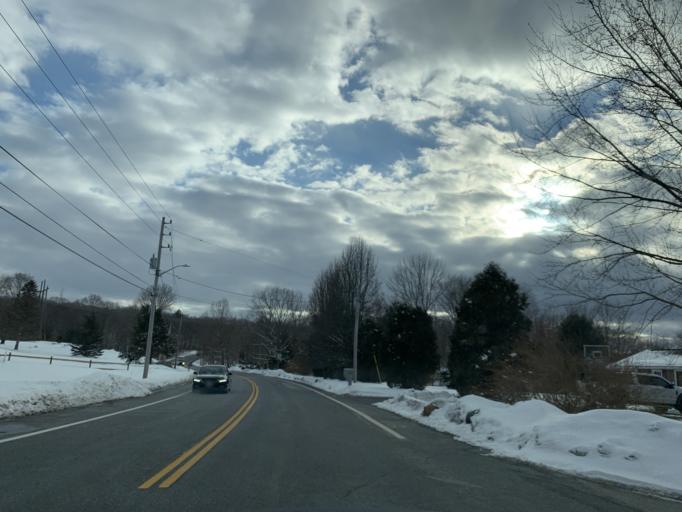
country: US
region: Rhode Island
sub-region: Providence County
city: Cumberland Hill
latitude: 42.0050
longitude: -71.4535
